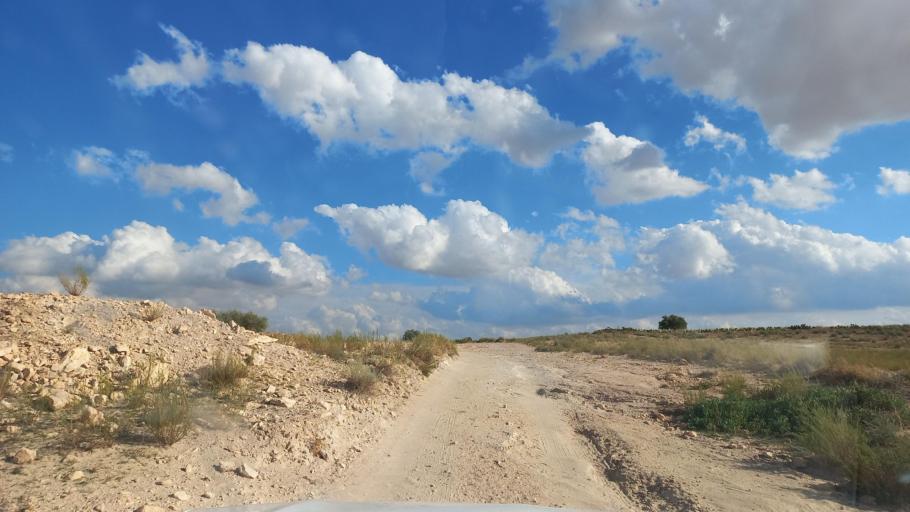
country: TN
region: Al Qasrayn
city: Sbiba
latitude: 35.3950
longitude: 9.0401
